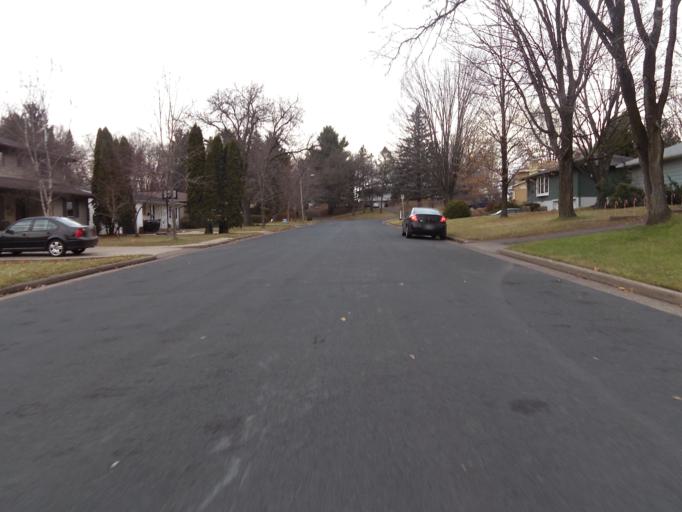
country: US
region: Wisconsin
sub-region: Pierce County
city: River Falls
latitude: 44.8536
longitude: -92.6134
